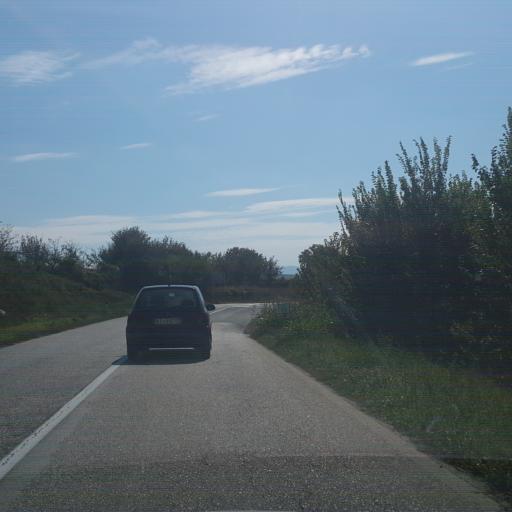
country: RS
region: Central Serbia
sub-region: Zajecarski Okrug
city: Knjazevac
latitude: 43.7252
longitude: 22.3098
